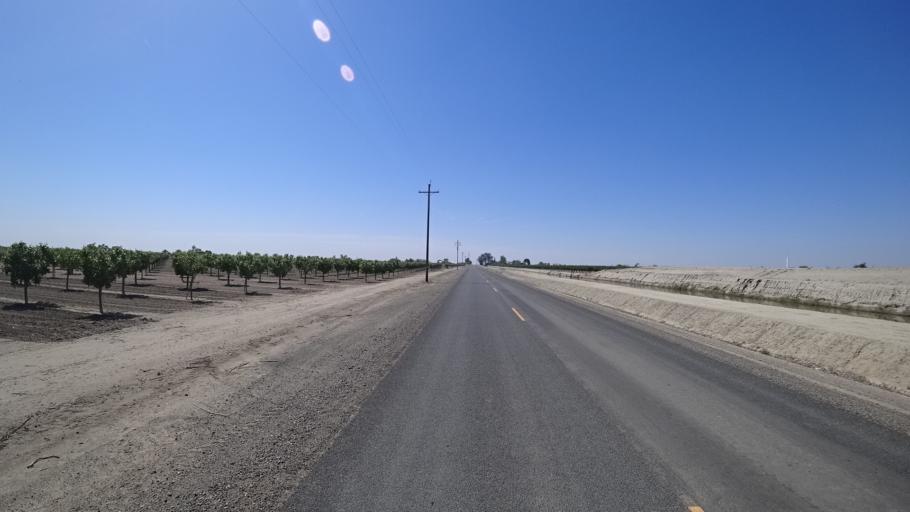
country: US
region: California
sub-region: Kings County
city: Corcoran
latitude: 36.0422
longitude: -119.5361
